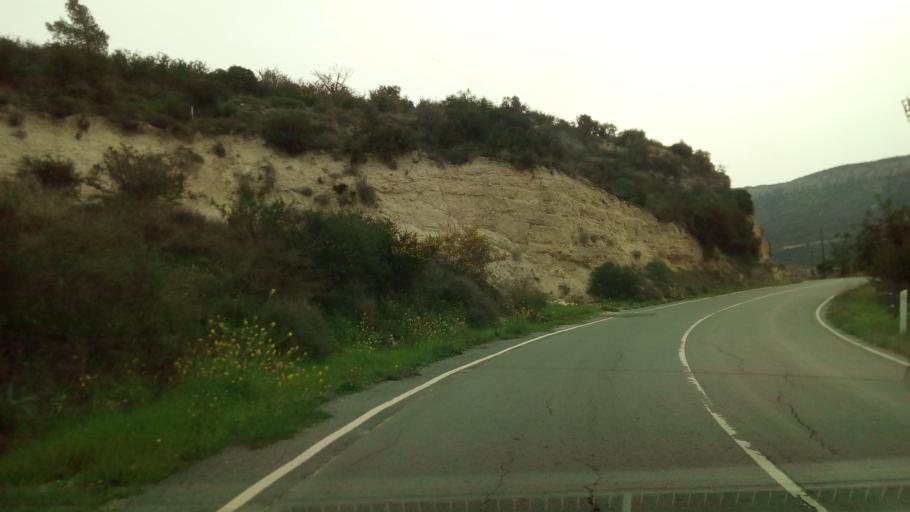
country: CY
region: Limassol
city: Mouttagiaka
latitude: 34.7519
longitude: 33.0826
